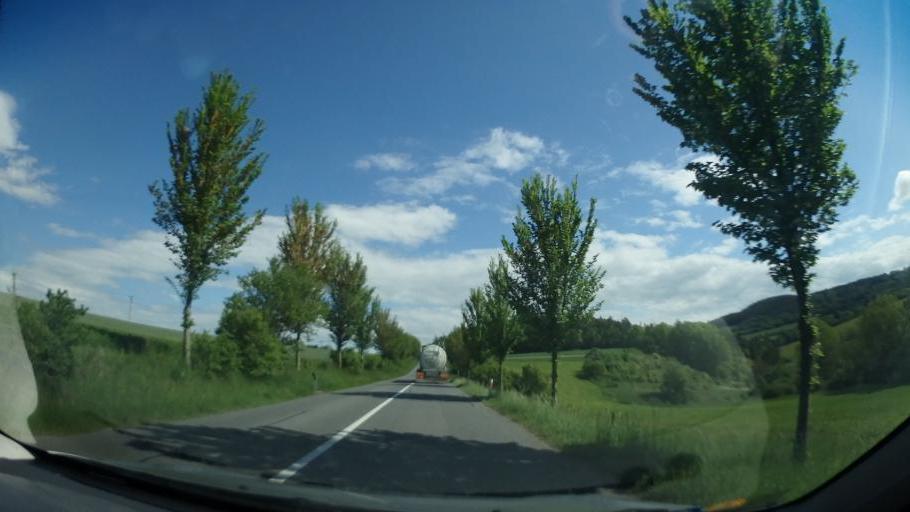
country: CZ
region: Pardubicky
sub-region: Okres Svitavy
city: Moravska Trebova
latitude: 49.7203
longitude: 16.6400
